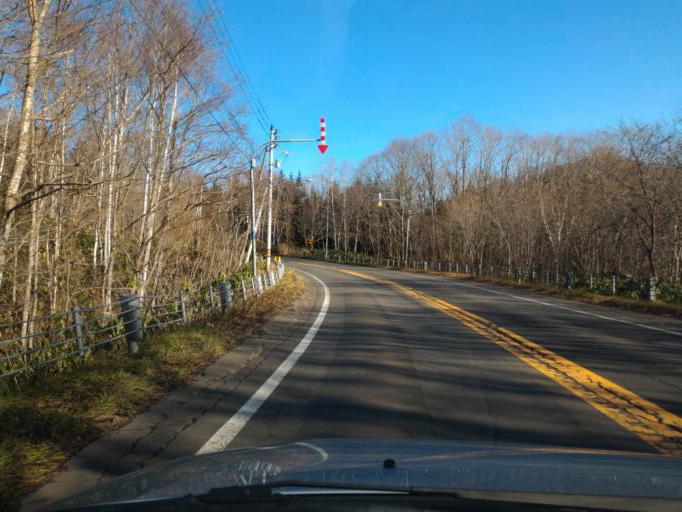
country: JP
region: Hokkaido
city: Bibai
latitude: 43.2631
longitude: 142.0310
